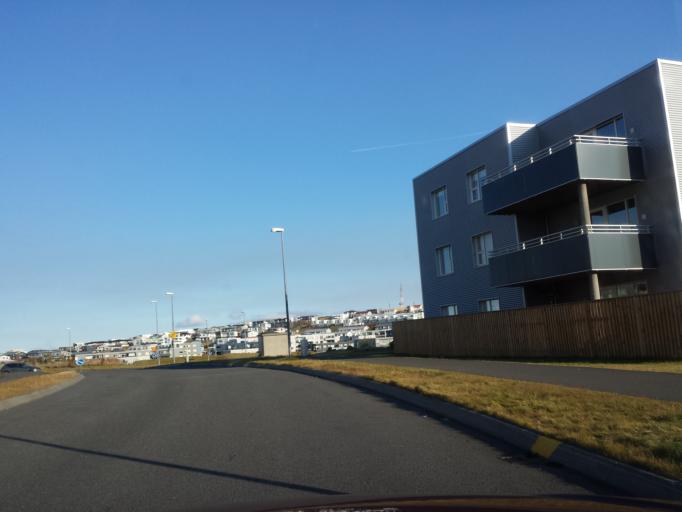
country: IS
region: Capital Region
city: Reykjavik
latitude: 64.0833
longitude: -21.8292
